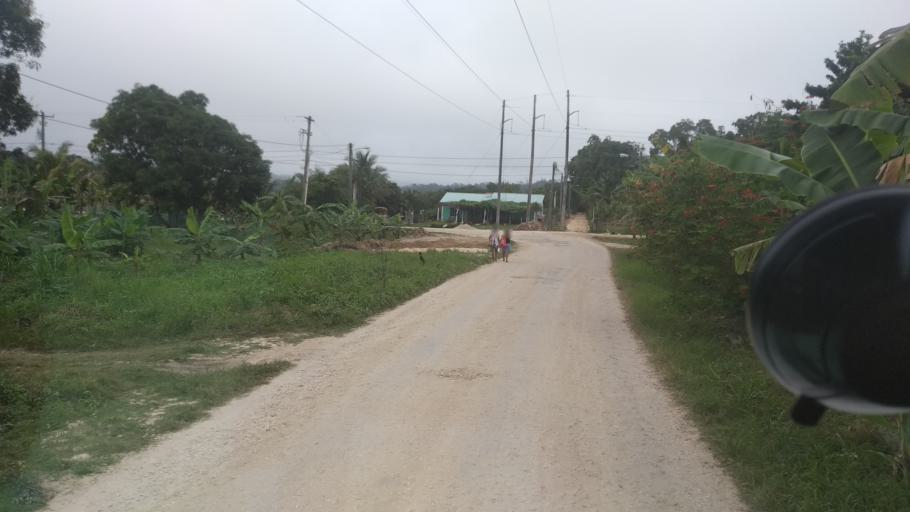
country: BZ
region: Cayo
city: Benque Viejo del Carmen
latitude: 17.0827
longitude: -89.1245
